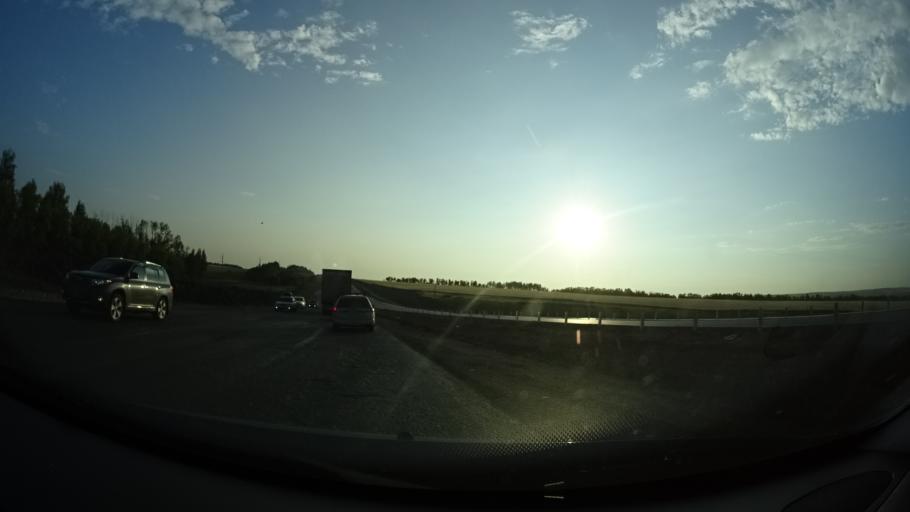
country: RU
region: Samara
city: Kamyshla
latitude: 54.0396
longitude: 51.9679
